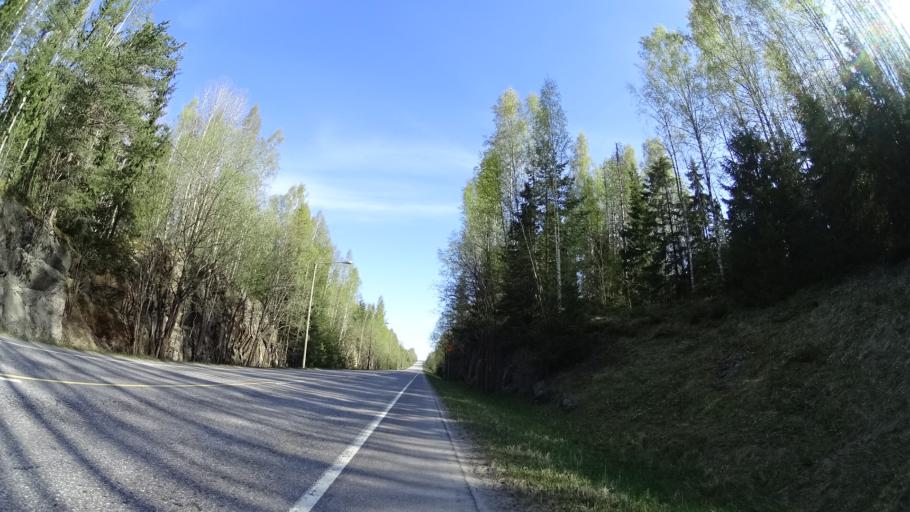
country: FI
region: Uusimaa
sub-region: Helsinki
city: Nurmijaervi
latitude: 60.3751
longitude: 24.8059
